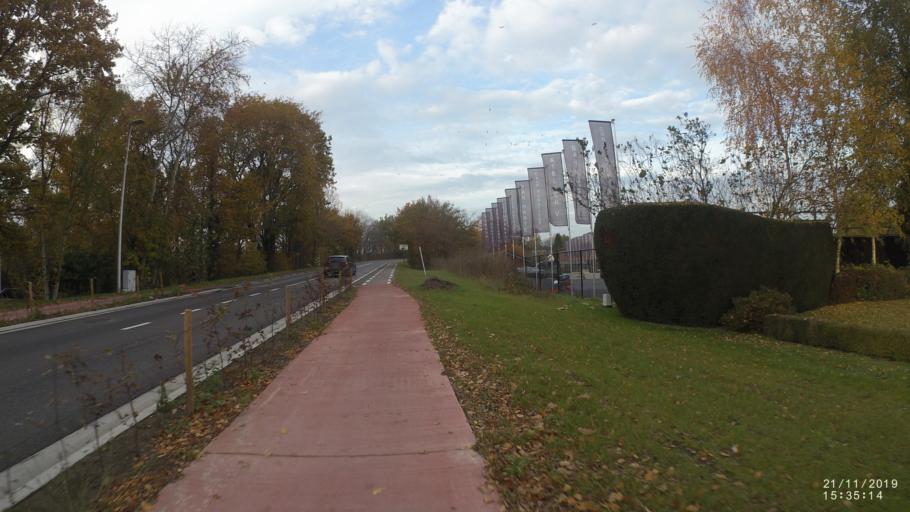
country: BE
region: Flanders
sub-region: Provincie Limburg
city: Hasselt
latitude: 50.9521
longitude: 5.3116
